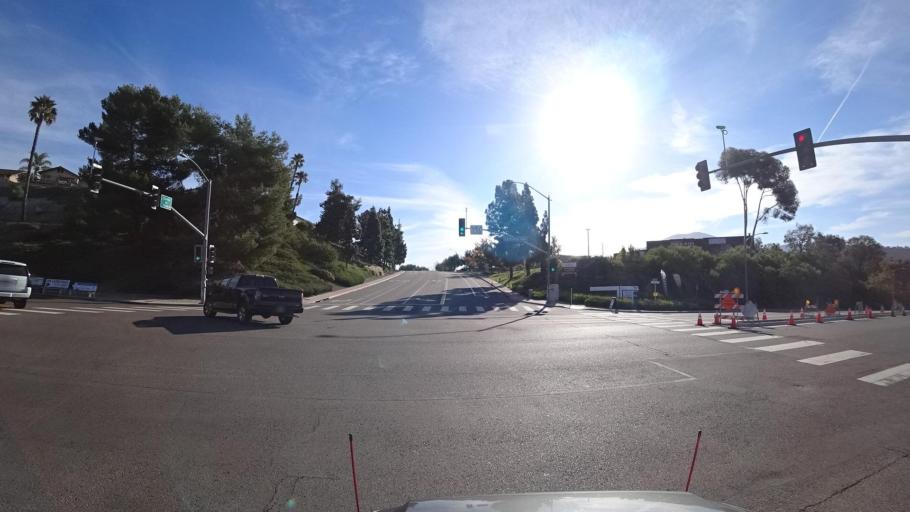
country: US
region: California
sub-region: San Diego County
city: Spring Valley
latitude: 32.7310
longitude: -116.9717
